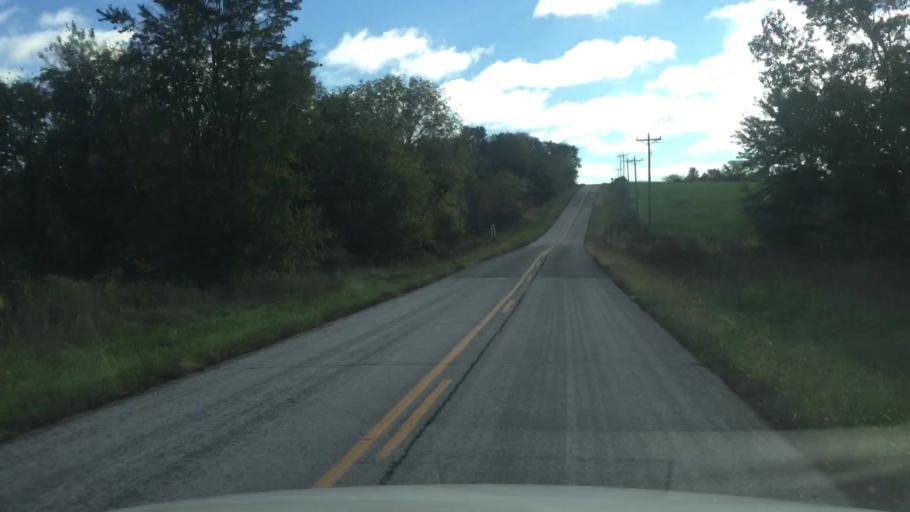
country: US
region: Missouri
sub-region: Howard County
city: Fayette
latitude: 39.1047
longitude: -92.7502
